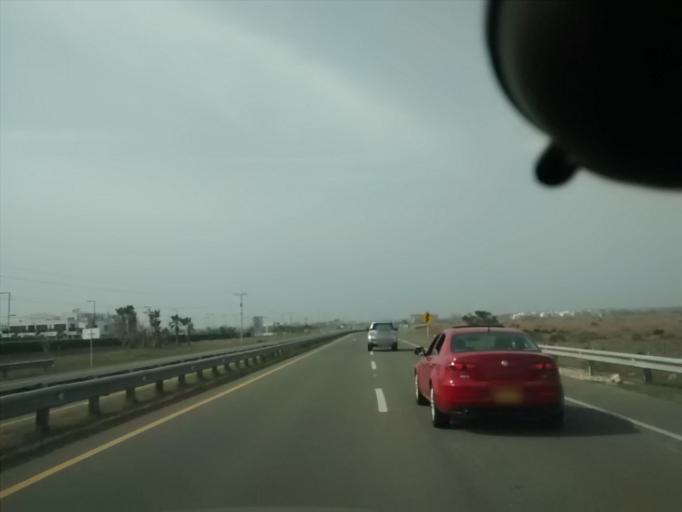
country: CO
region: Bolivar
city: Santa Rosa
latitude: 10.5201
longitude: -75.4670
